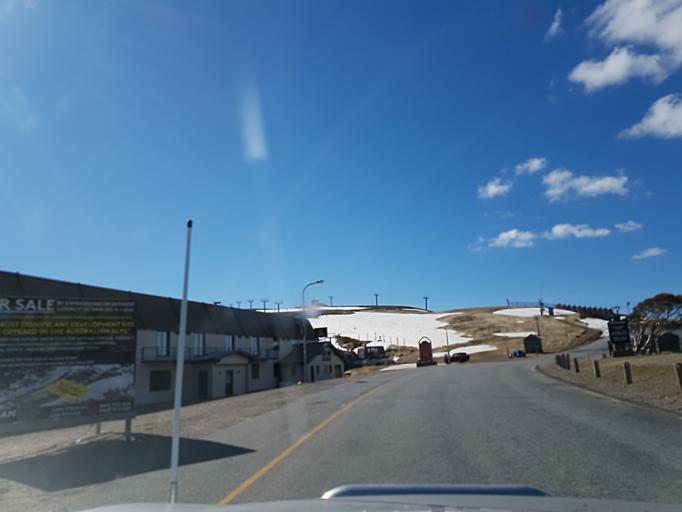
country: AU
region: Victoria
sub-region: Alpine
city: Mount Beauty
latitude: -36.9822
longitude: 147.1423
